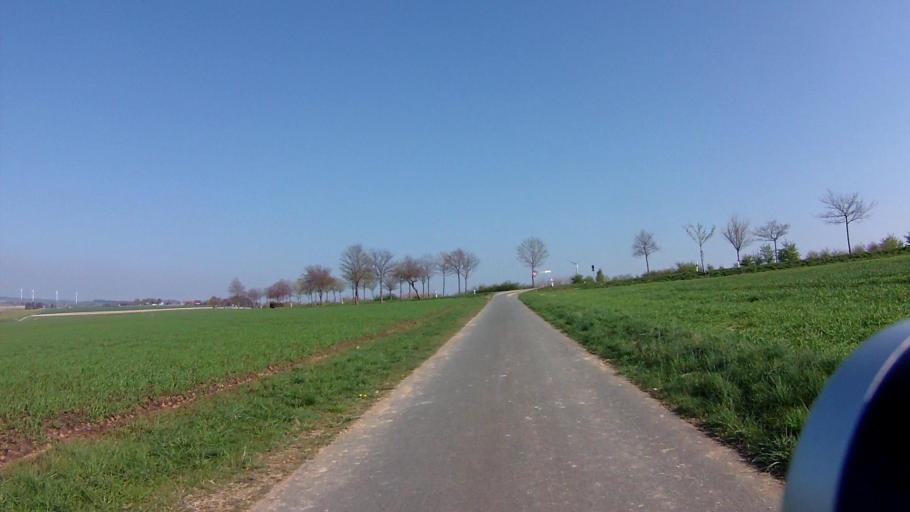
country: DE
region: North Rhine-Westphalia
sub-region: Regierungsbezirk Detmold
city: Paderborn
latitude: 51.6996
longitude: 8.8135
